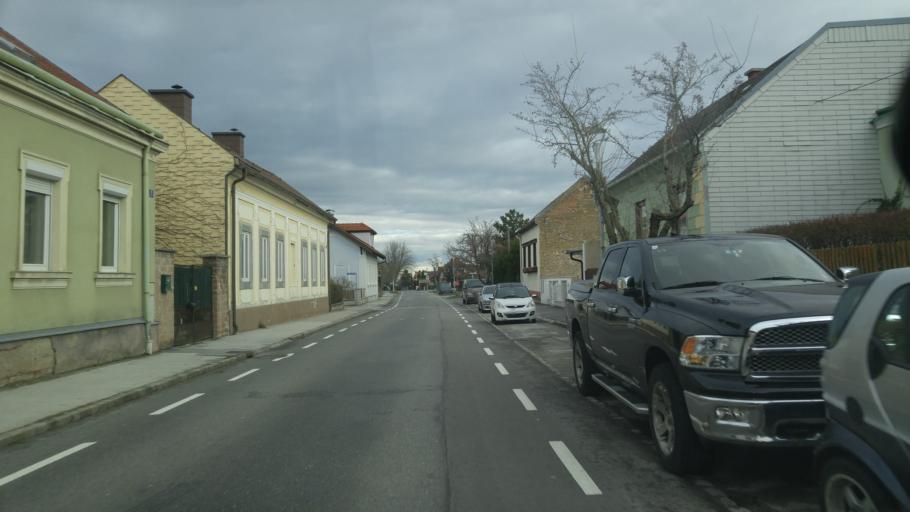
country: AT
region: Lower Austria
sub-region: Politischer Bezirk Baden
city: Bad Voslau
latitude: 47.9592
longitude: 16.2037
